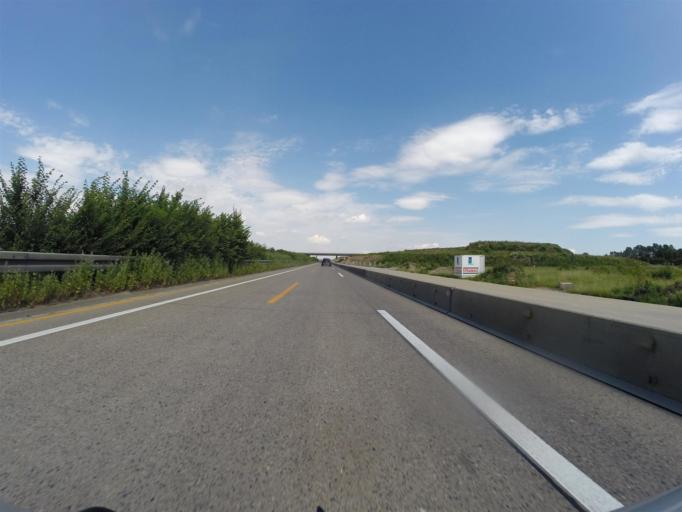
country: DE
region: Lower Saxony
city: Seesen
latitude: 51.9450
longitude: 10.1439
